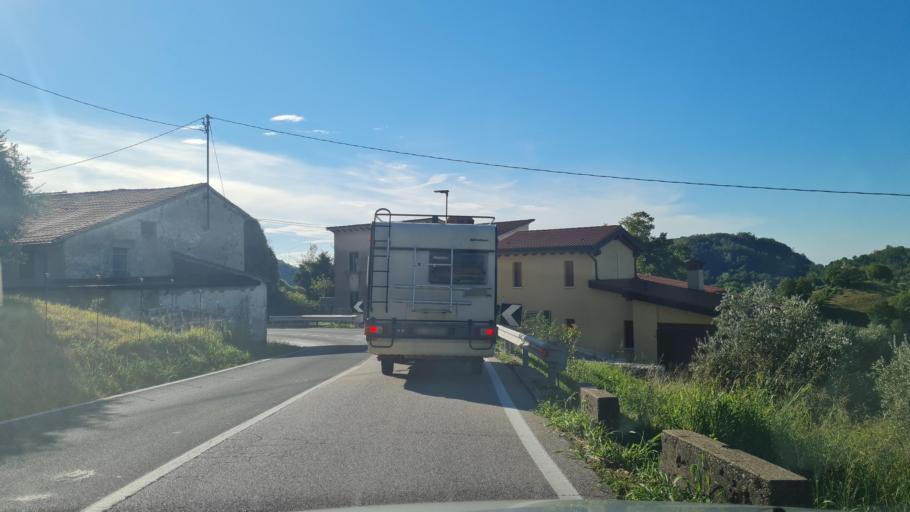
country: IT
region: Veneto
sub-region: Provincia di Vicenza
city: Marostica
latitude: 45.7785
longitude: 11.6828
